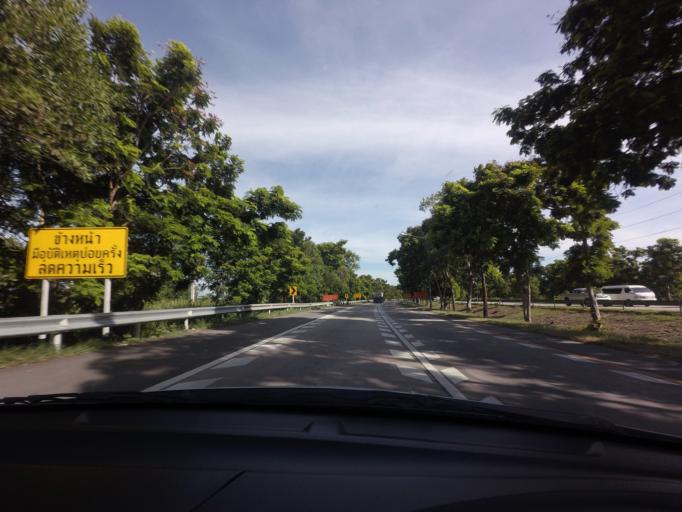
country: TH
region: Suphan Buri
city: Bang Pla Ma
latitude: 14.3421
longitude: 100.1914
